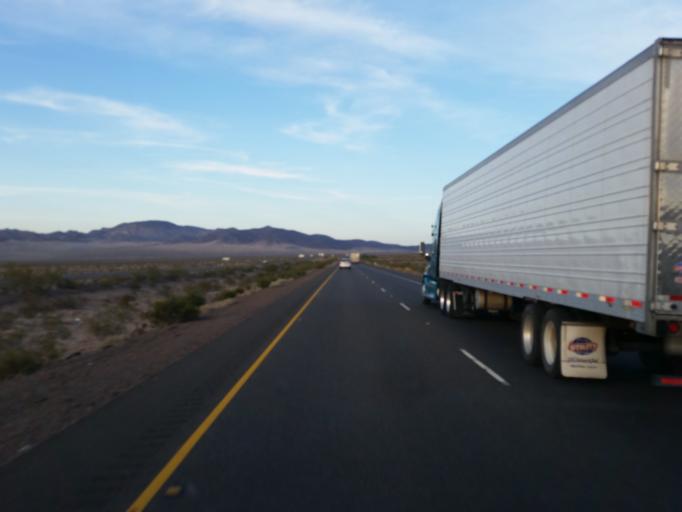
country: US
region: California
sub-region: San Bernardino County
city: Twentynine Palms
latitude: 34.7257
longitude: -116.1568
